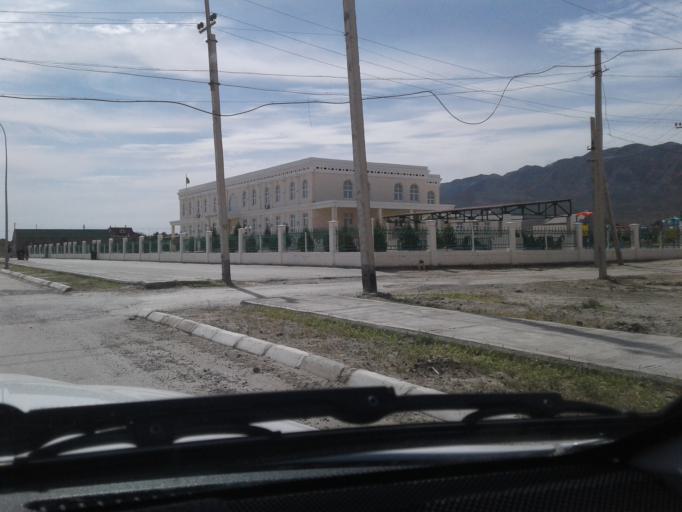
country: TM
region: Balkan
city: Gazanjyk
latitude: 39.2438
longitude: 55.4991
